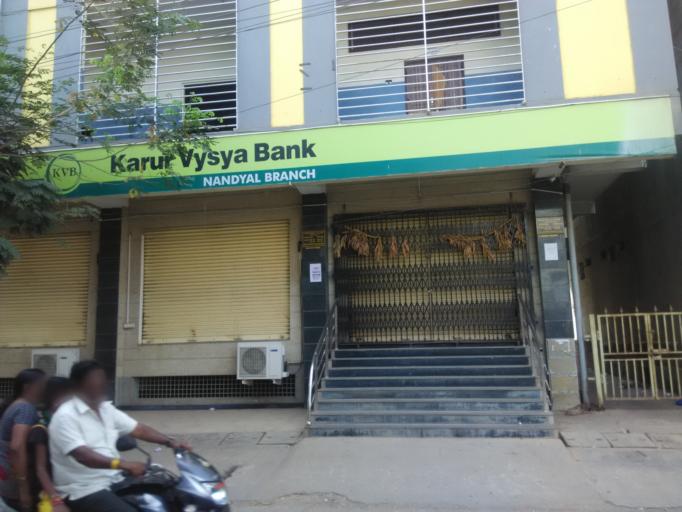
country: IN
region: Andhra Pradesh
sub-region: Kurnool
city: Nandyal
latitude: 15.4864
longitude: 78.4812
